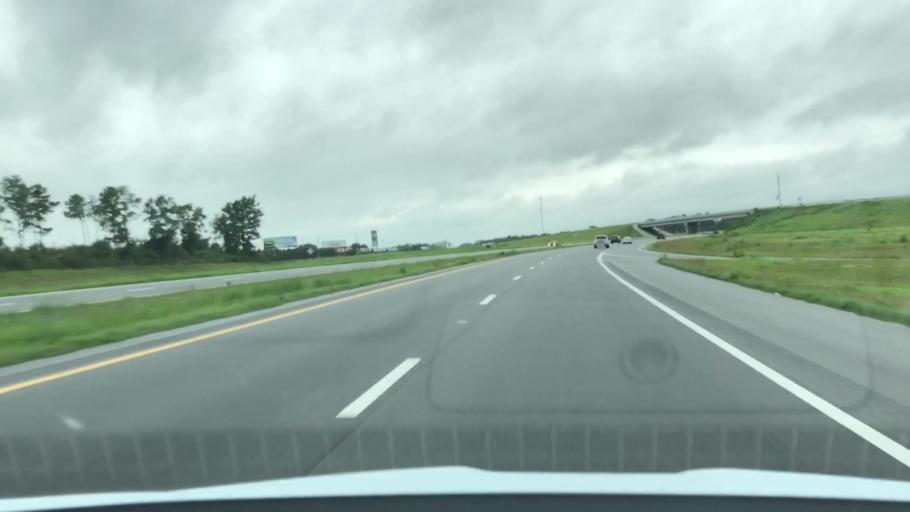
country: US
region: North Carolina
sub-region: Lenoir County
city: La Grange
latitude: 35.3013
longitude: -77.8159
